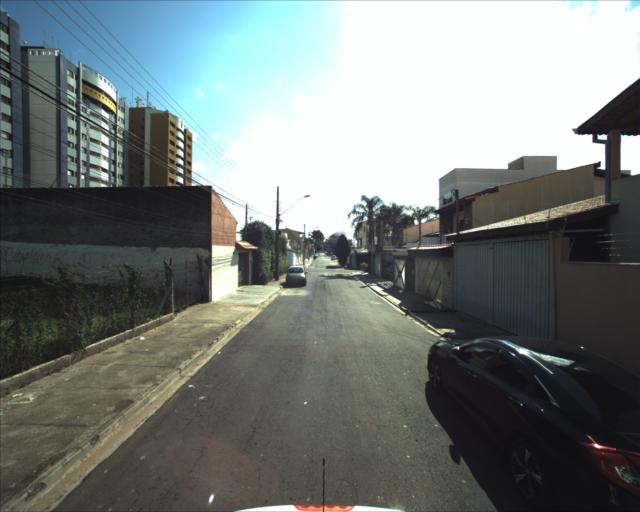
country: BR
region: Sao Paulo
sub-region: Sorocaba
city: Sorocaba
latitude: -23.4861
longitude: -47.4755
